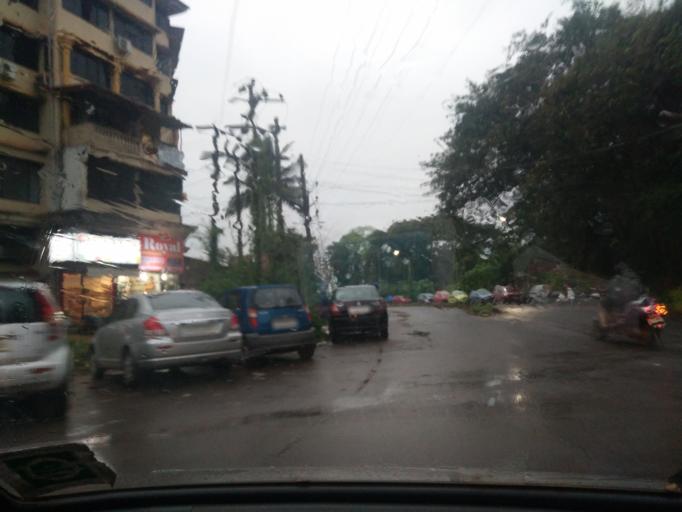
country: IN
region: Goa
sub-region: South Goa
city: Madgaon
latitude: 15.2895
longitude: 73.9544
